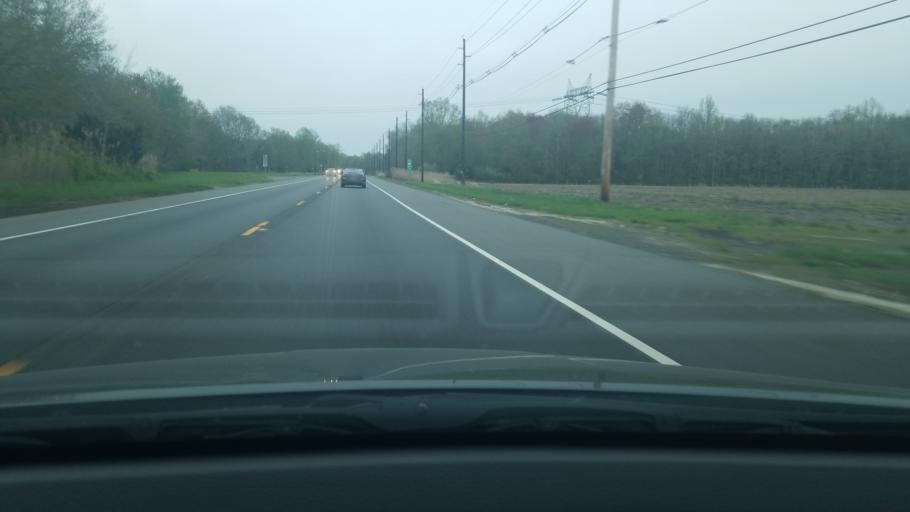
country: US
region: New Jersey
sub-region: Burlington County
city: Medford Lakes
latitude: 39.8930
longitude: -74.7705
